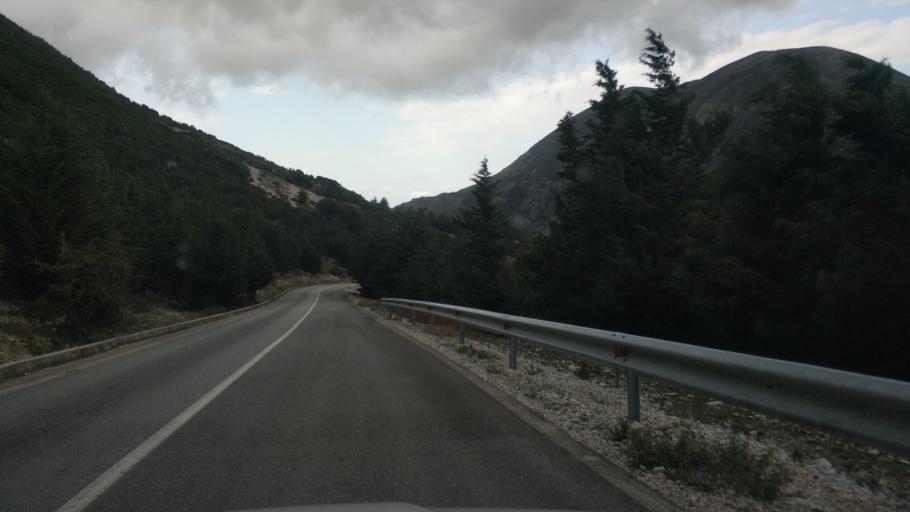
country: AL
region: Vlore
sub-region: Rrethi i Vlores
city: Orikum
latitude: 40.2397
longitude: 19.5514
